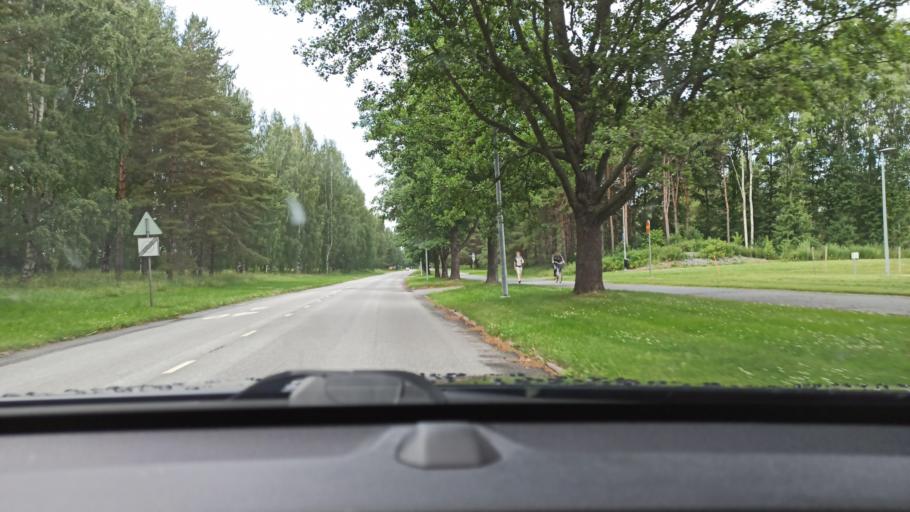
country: FI
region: Satakunta
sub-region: Pori
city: Pori
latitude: 61.4993
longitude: 21.7854
